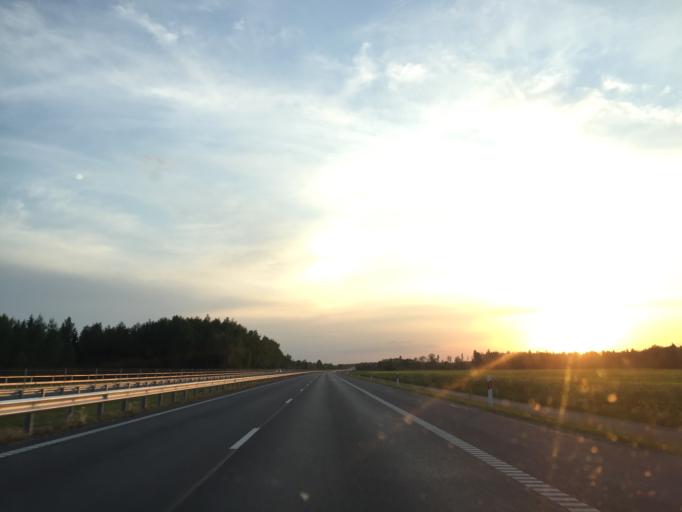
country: LT
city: Kursenai
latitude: 55.9845
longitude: 23.0985
